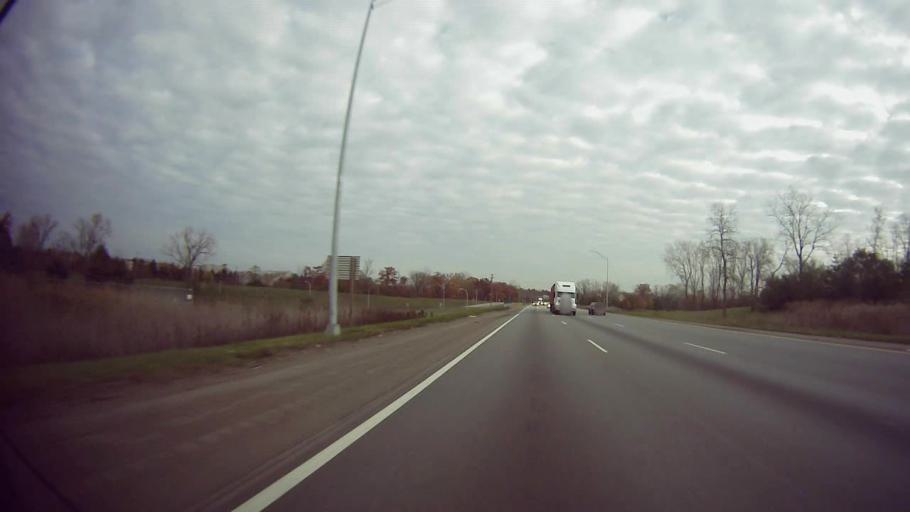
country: US
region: Michigan
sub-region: Wayne County
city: Taylor
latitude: 42.2536
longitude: -83.3040
